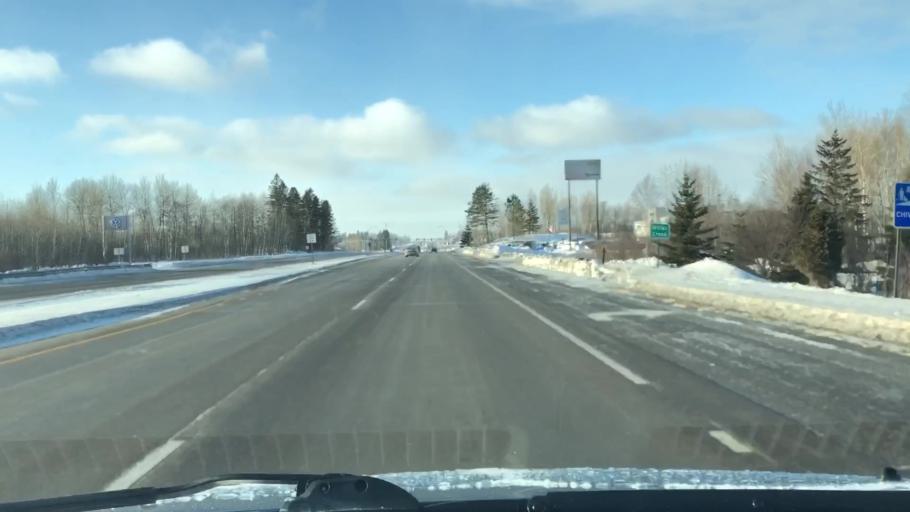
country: US
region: Minnesota
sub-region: Saint Louis County
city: Hermantown
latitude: 46.8167
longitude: -92.1778
